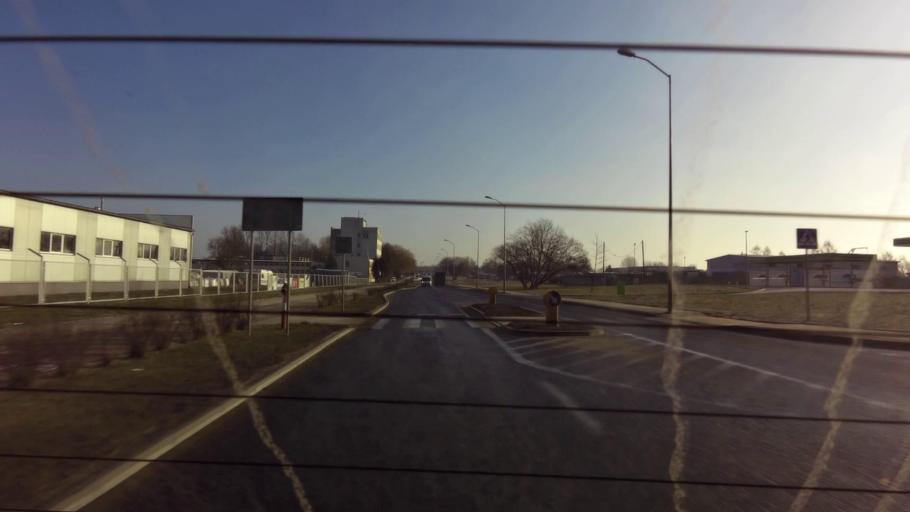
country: PL
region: West Pomeranian Voivodeship
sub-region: Koszalin
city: Koszalin
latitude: 54.1755
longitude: 16.1763
